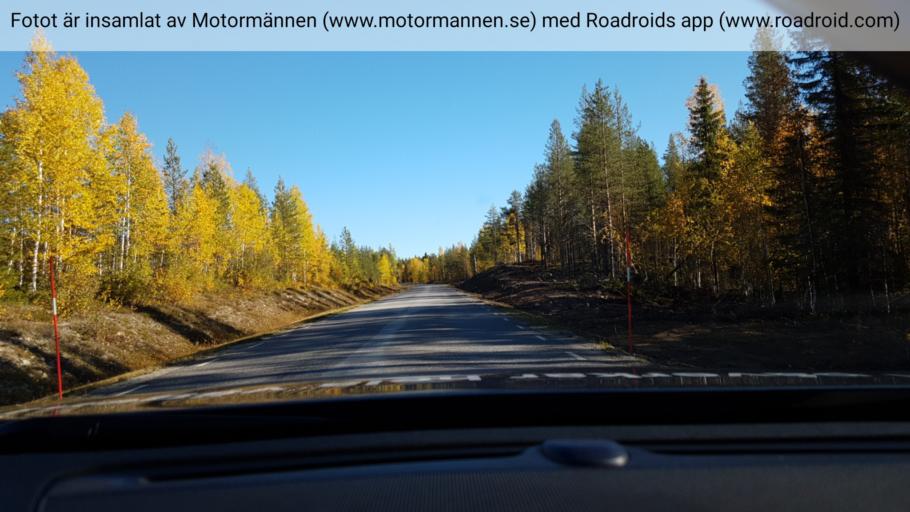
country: SE
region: Norrbotten
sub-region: Gallivare Kommun
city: Gaellivare
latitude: 66.4665
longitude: 20.8272
